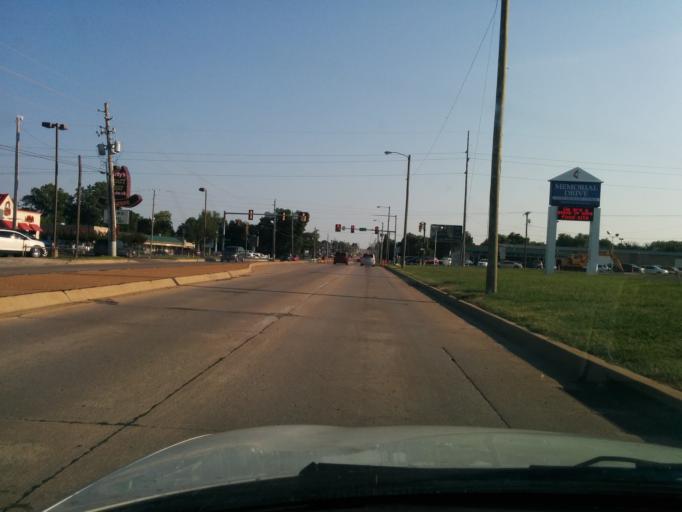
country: US
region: Oklahoma
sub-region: Tulsa County
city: Tulsa
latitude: 36.1416
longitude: -95.8868
